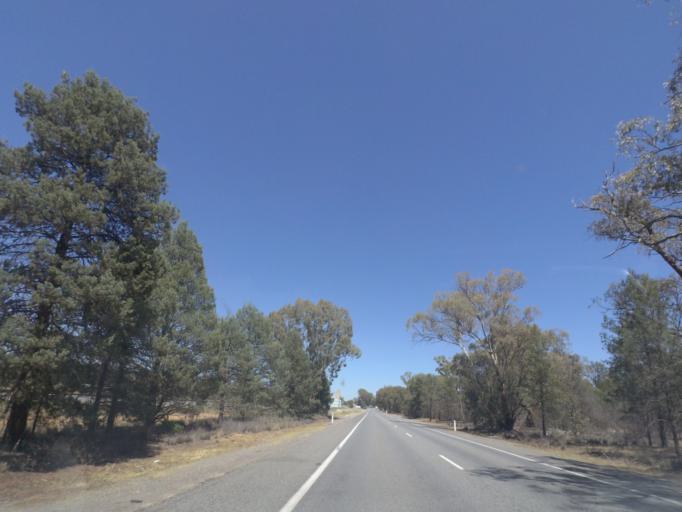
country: AU
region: New South Wales
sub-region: Narrandera
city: Narrandera
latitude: -34.7384
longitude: 146.5768
